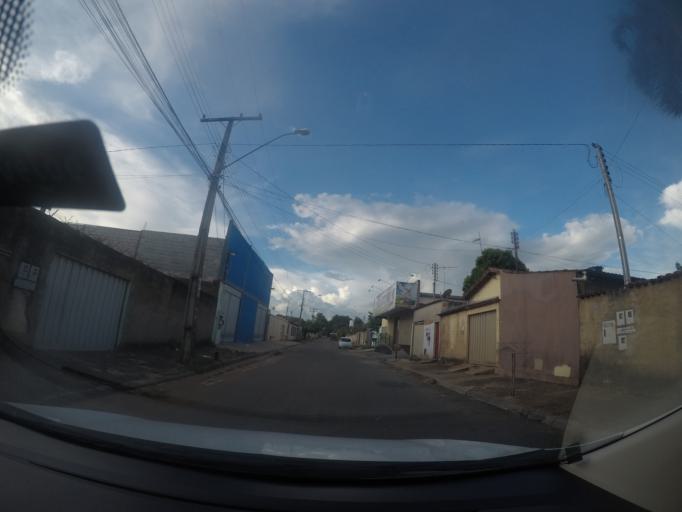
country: BR
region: Goias
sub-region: Goiania
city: Goiania
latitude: -16.6881
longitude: -49.3195
